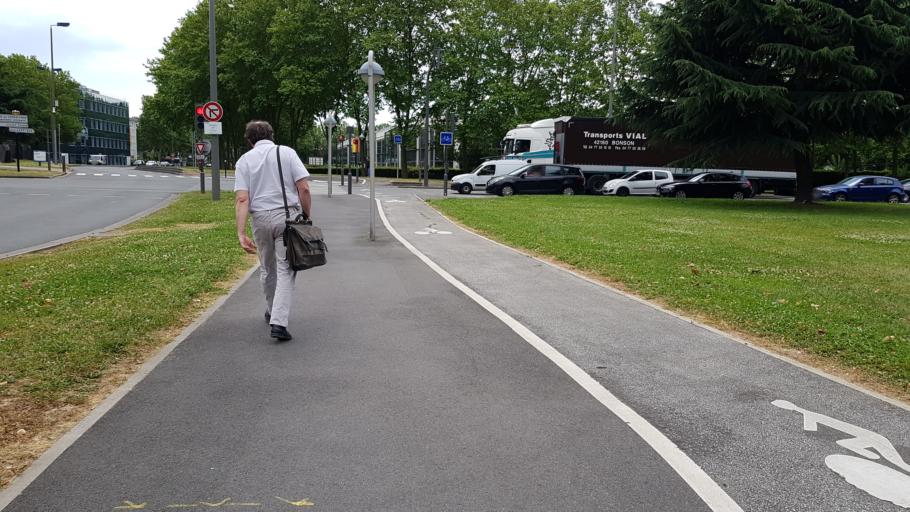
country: FR
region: Ile-de-France
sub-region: Departement de Seine-Saint-Denis
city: Villepinte
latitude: 48.9742
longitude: 2.5082
